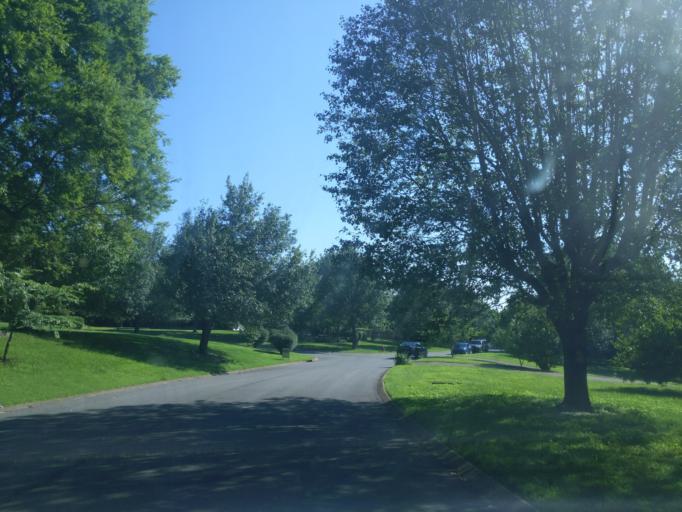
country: US
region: Tennessee
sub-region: Williamson County
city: Brentwood Estates
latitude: 36.0215
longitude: -86.7567
